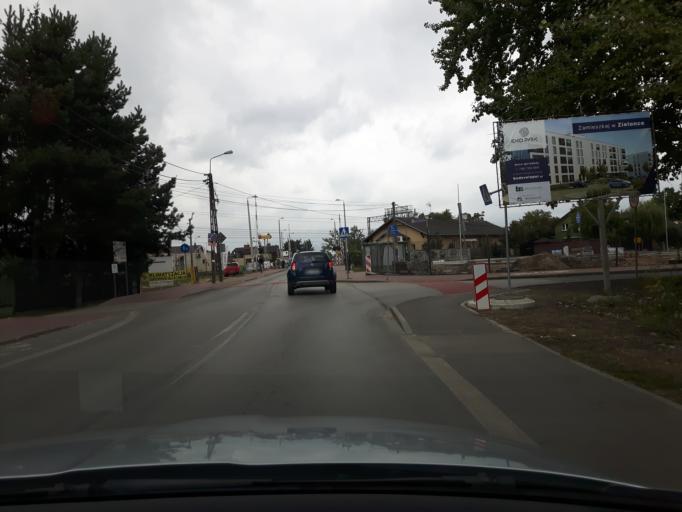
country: PL
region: Masovian Voivodeship
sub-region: Powiat wolominski
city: Kobylka
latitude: 52.3255
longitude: 21.1912
